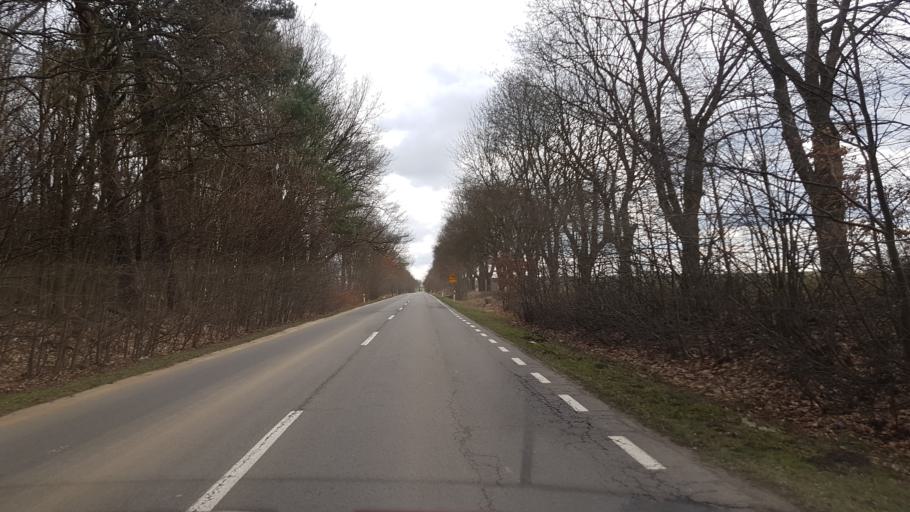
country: PL
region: West Pomeranian Voivodeship
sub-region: Powiat gryfinski
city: Banie
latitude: 53.1601
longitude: 14.5981
